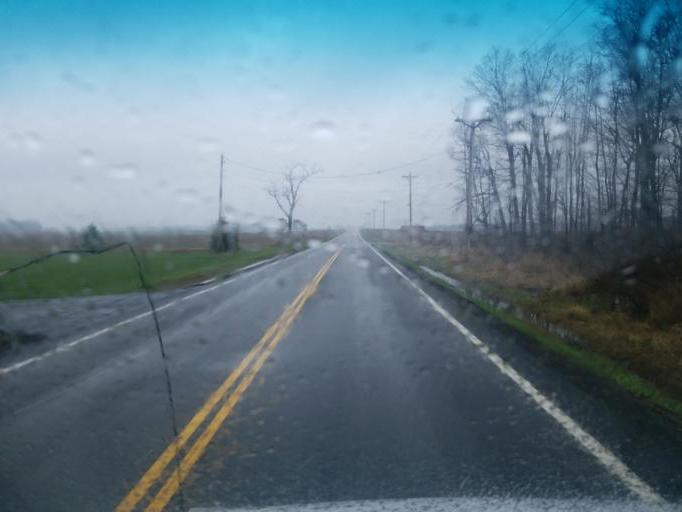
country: US
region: Ohio
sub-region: Crawford County
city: Bucyrus
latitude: 40.9651
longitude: -82.9223
